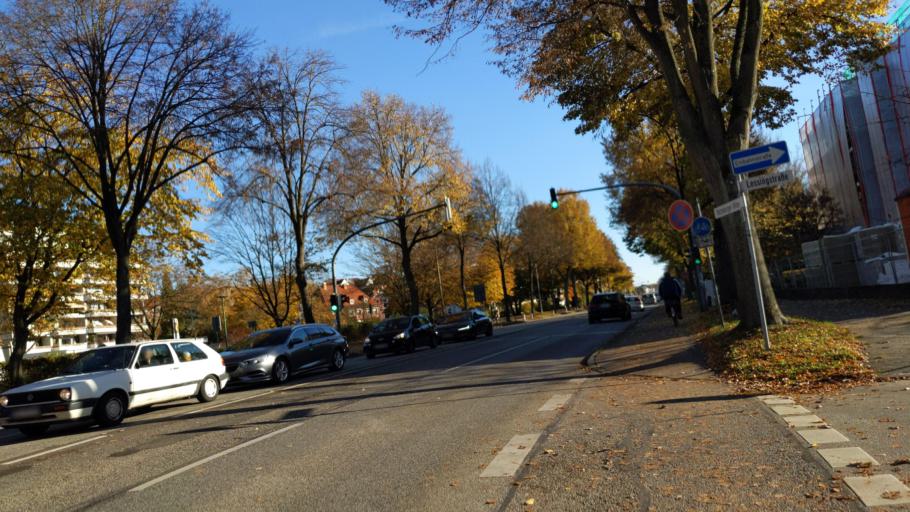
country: DE
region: Schleswig-Holstein
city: Luebeck
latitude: 53.8573
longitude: 10.6945
